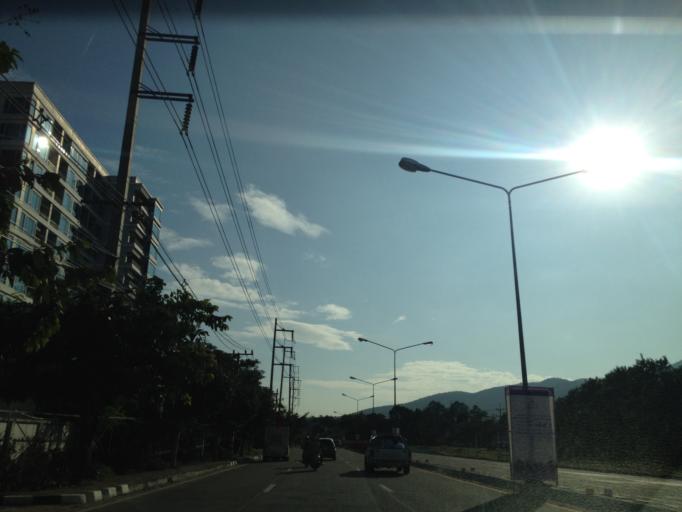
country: TH
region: Chiang Mai
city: Chiang Mai
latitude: 18.8198
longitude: 98.9642
